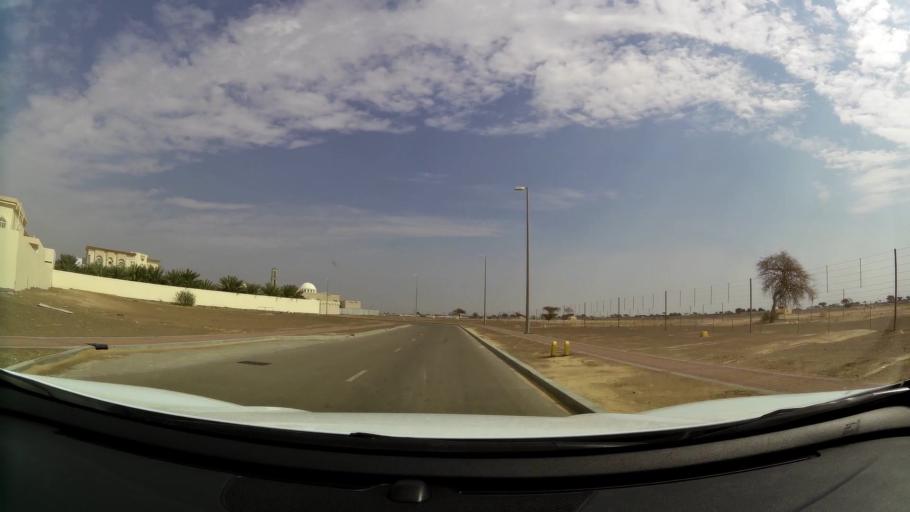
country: AE
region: Abu Dhabi
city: Al Ain
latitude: 24.1856
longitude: 55.8002
